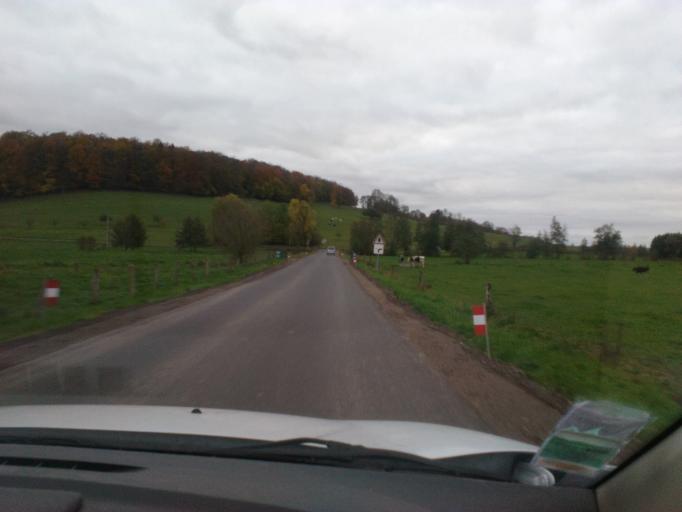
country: FR
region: Lorraine
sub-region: Departement des Vosges
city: Mirecourt
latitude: 48.2770
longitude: 6.2339
